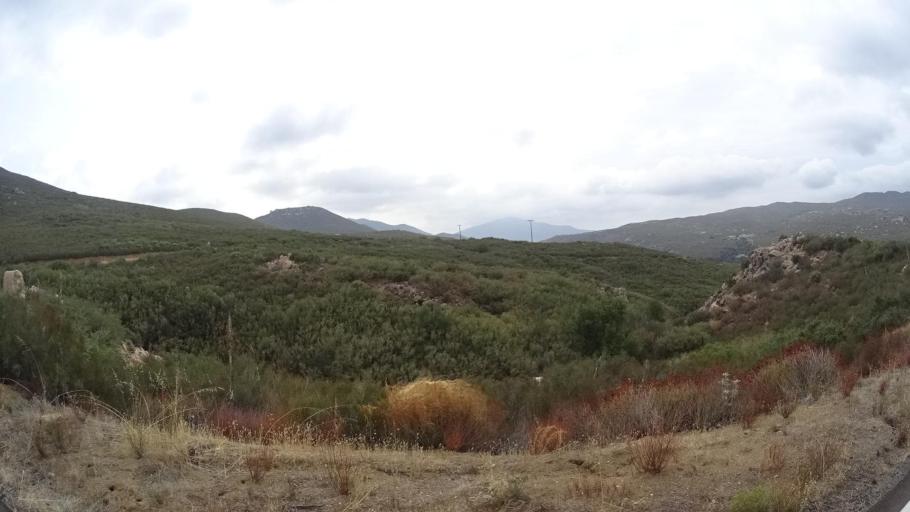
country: US
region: California
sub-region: San Diego County
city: Descanso
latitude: 32.8964
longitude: -116.6463
